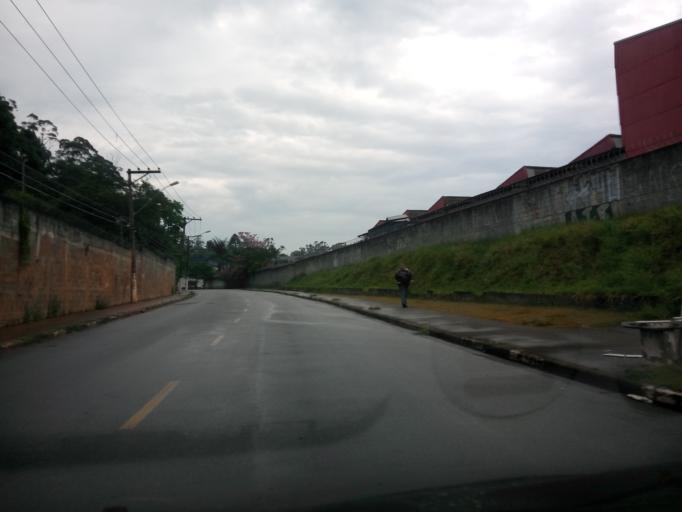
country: BR
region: Sao Paulo
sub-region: Sao Bernardo Do Campo
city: Sao Bernardo do Campo
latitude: -23.7256
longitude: -46.5929
